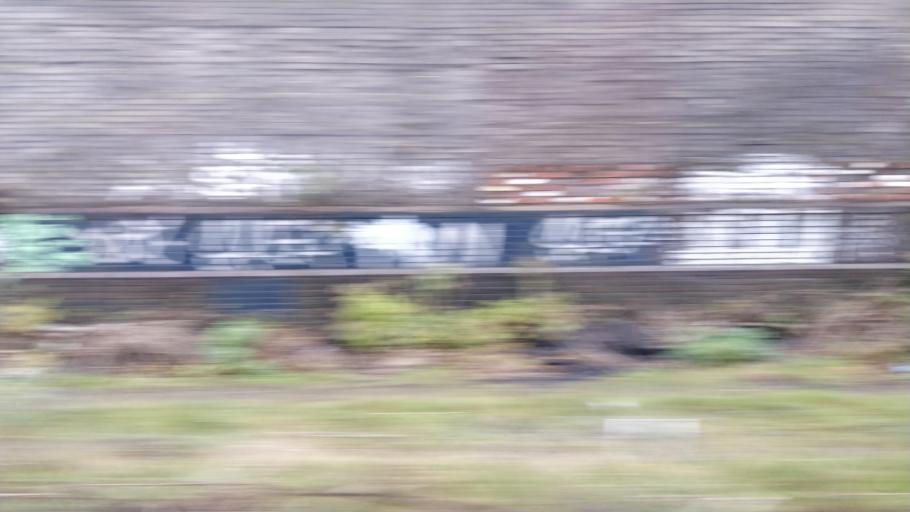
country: GB
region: England
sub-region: City and Borough of Salford
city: Salford
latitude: 53.4933
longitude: -2.2855
